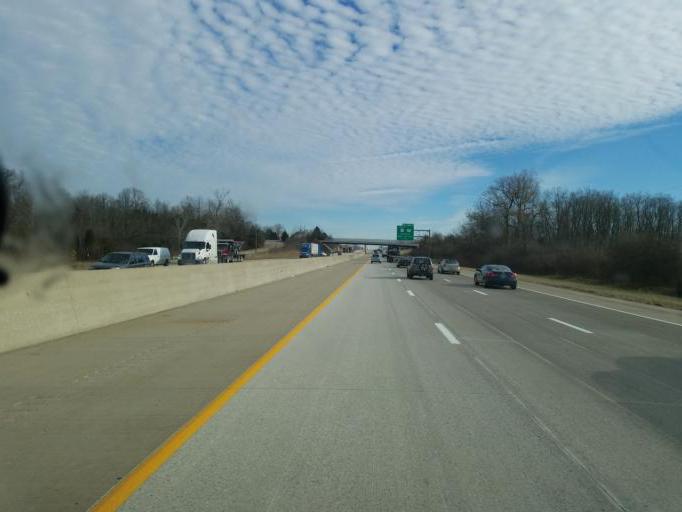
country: US
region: Ohio
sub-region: Montgomery County
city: Huber Heights
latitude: 39.8667
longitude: -84.0835
